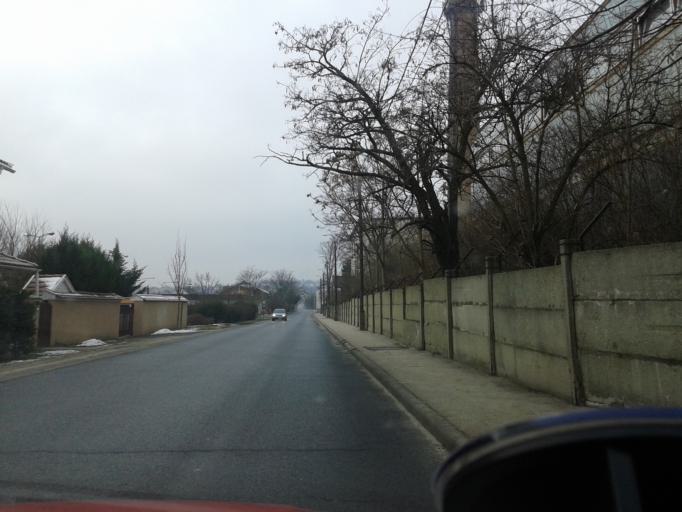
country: HU
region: Pest
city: Diosd
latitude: 47.4060
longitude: 18.9432
